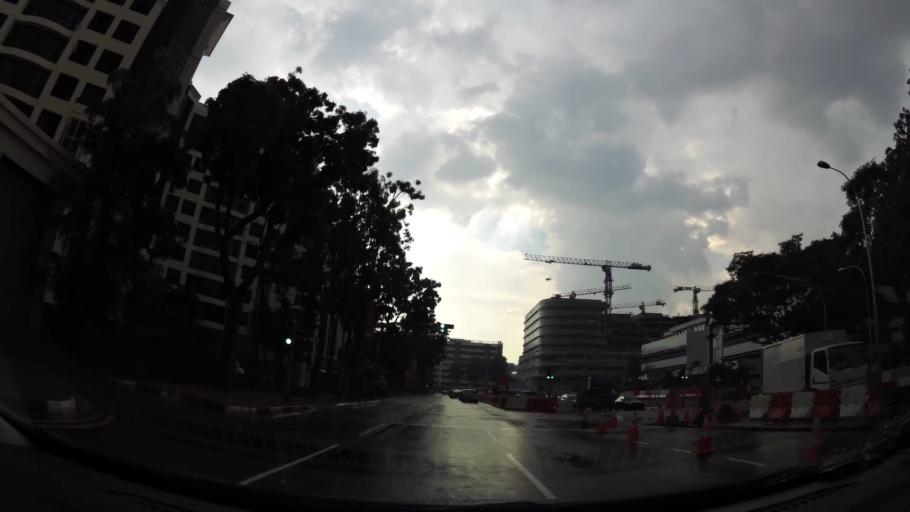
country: SG
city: Singapore
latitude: 1.3402
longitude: 103.9511
